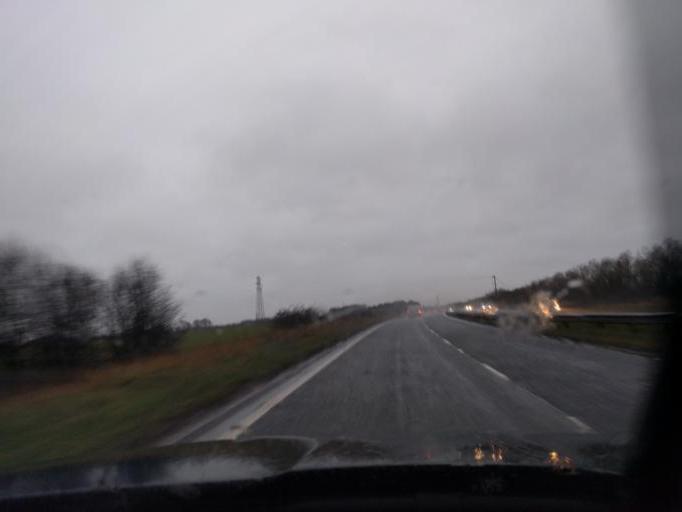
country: GB
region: England
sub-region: Northumberland
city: Bedlington
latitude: 55.1171
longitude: -1.5570
